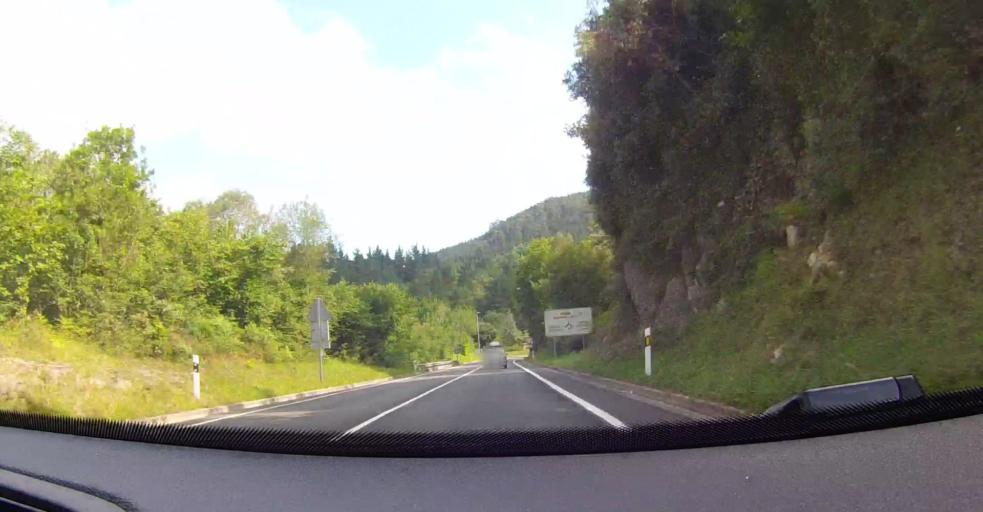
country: ES
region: Basque Country
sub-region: Bizkaia
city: Ibarrangelu
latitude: 43.3610
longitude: -2.6386
